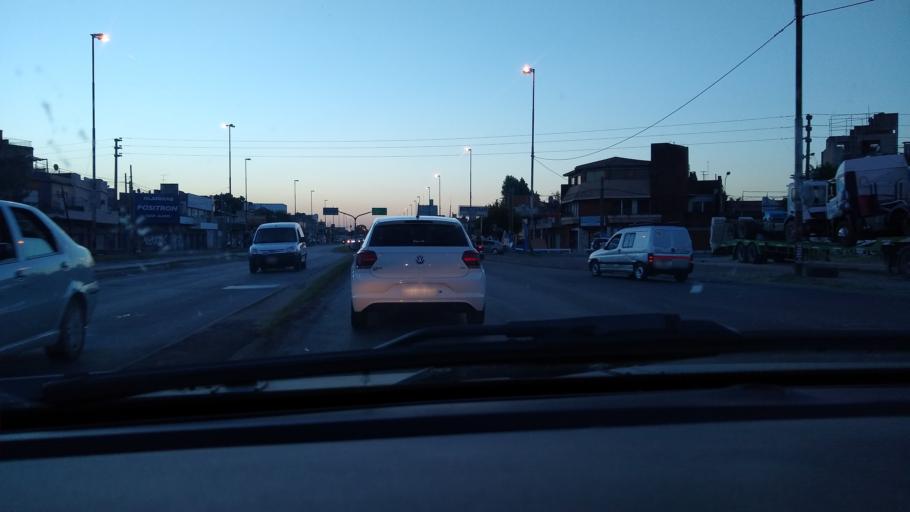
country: AR
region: Buenos Aires
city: San Justo
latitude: -34.6825
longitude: -58.5720
